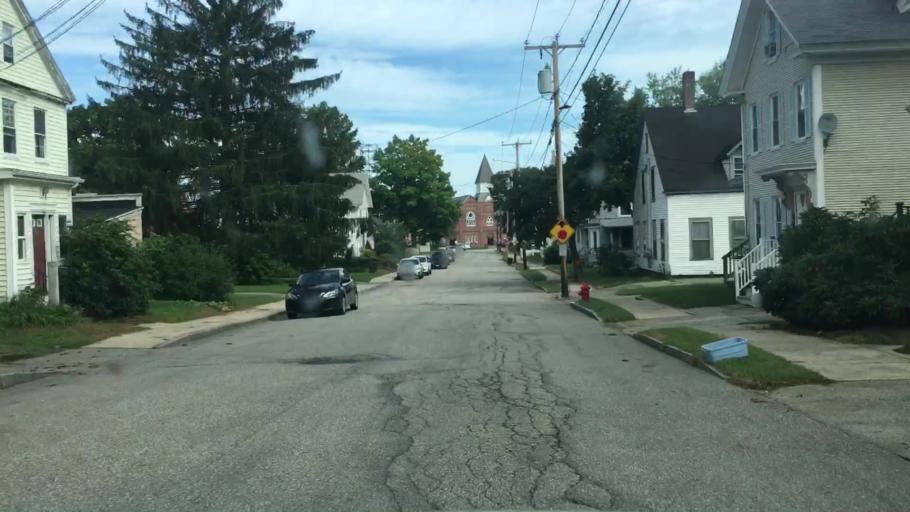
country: US
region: New Hampshire
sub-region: Strafford County
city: Dover
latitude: 43.1924
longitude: -70.8778
